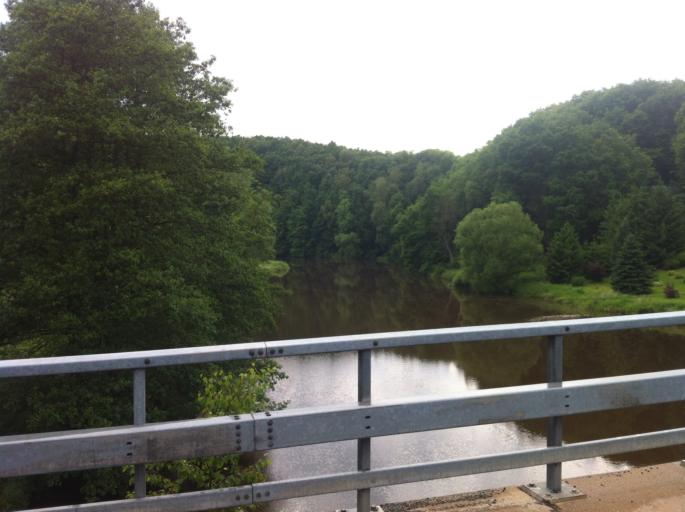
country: DE
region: Saxony
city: Lunzenau
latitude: 50.9794
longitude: 12.7647
